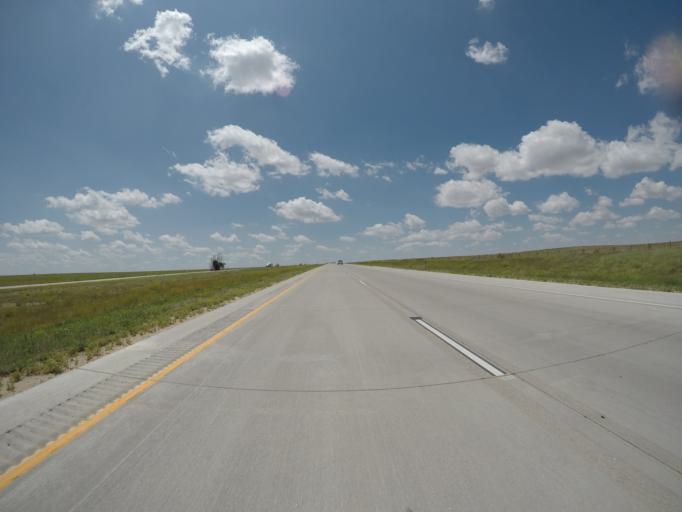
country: US
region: Colorado
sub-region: Kit Carson County
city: Burlington
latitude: 39.2940
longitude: -102.7502
